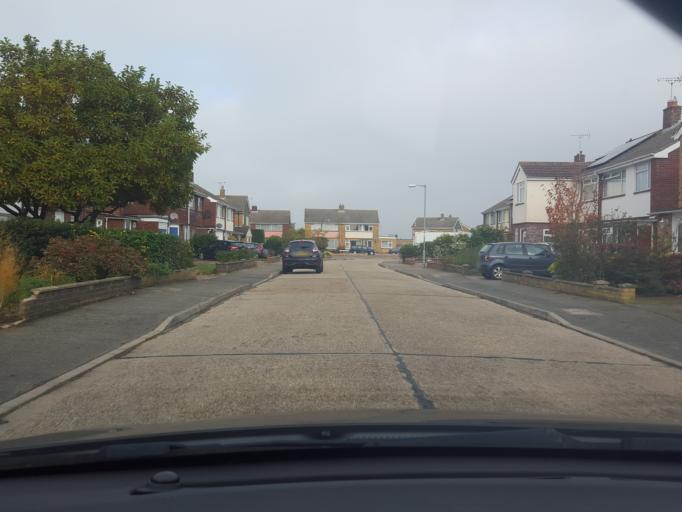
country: GB
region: England
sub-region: Essex
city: Manningtree
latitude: 51.9394
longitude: 1.0483
